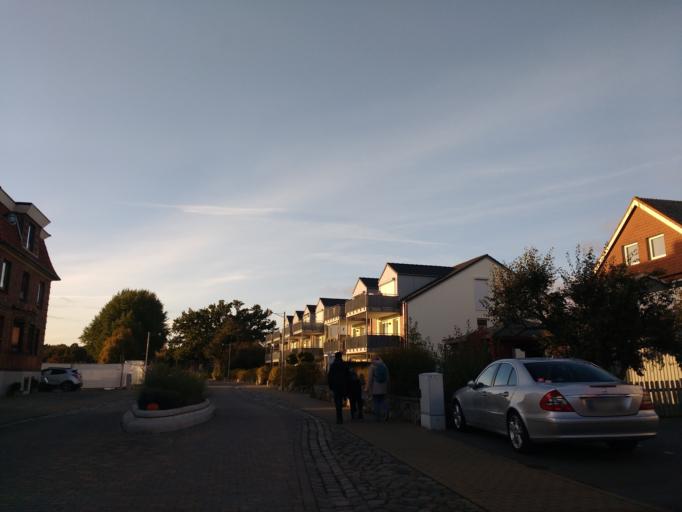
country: DE
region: Schleswig-Holstein
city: Kellenhusen
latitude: 54.1918
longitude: 11.0580
